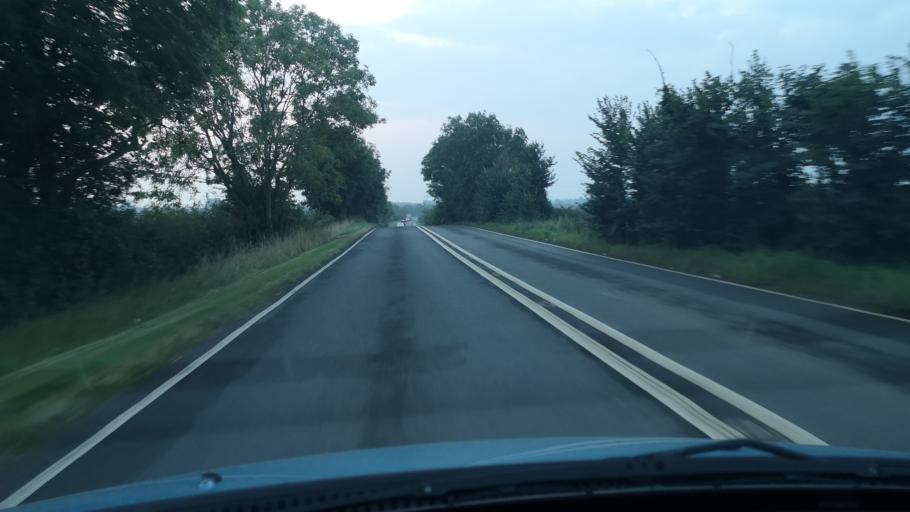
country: GB
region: England
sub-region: City and Borough of Wakefield
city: Badsworth
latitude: 53.6168
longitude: -1.3047
